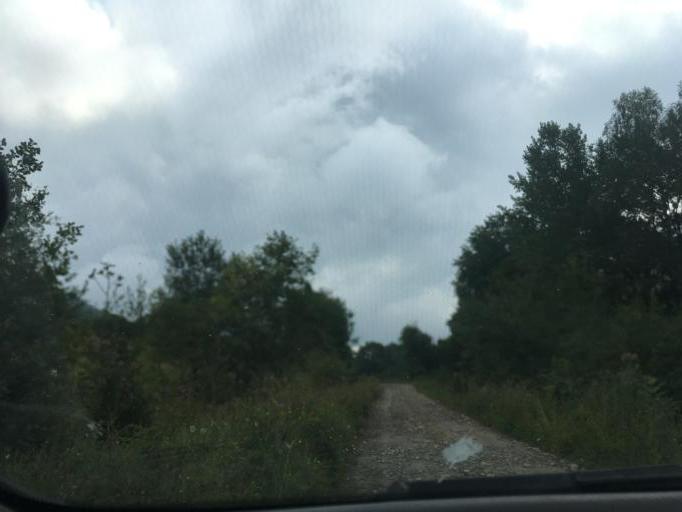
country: PL
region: Subcarpathian Voivodeship
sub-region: Powiat bieszczadzki
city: Lutowiska
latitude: 49.1645
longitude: 22.6225
